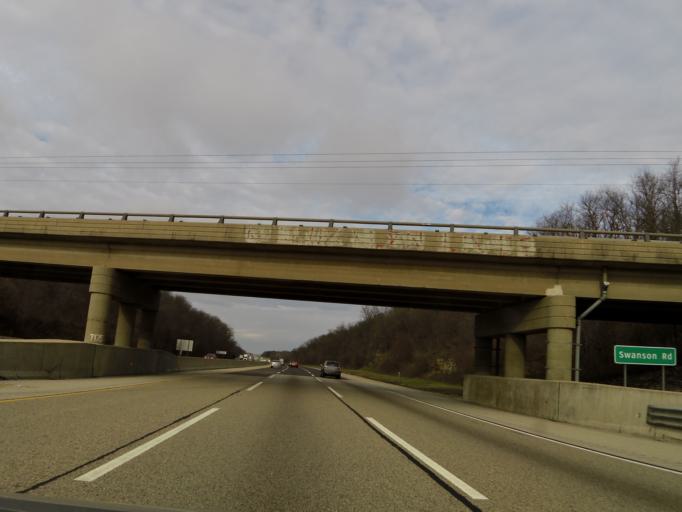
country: US
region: Illinois
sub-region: Winnebago County
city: Roscoe
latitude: 42.3883
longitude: -88.9744
